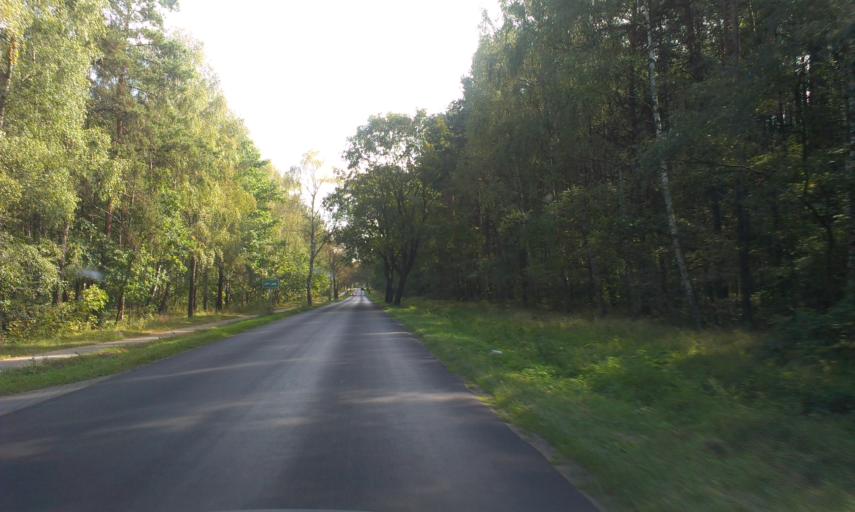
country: PL
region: Greater Poland Voivodeship
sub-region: Powiat zlotowski
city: Zlotow
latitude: 53.3533
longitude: 17.0547
